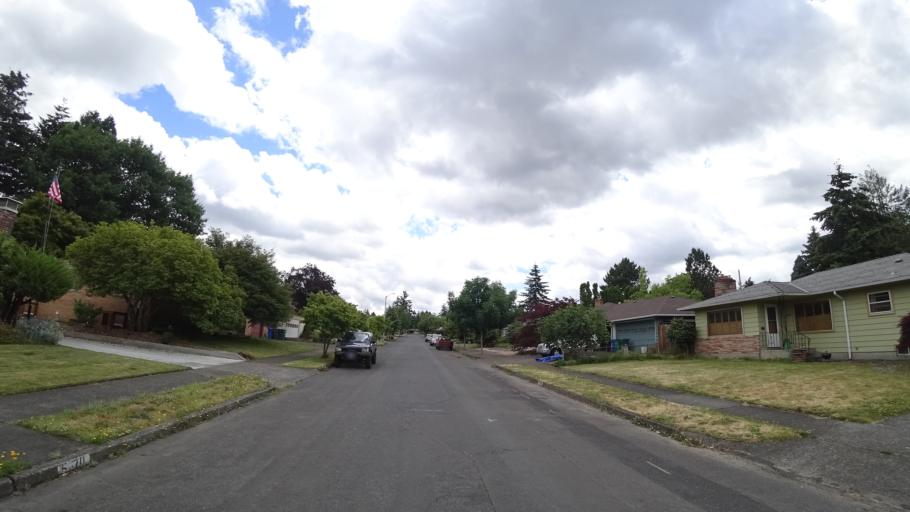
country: US
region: Oregon
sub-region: Multnomah County
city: Portland
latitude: 45.5618
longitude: -122.6120
